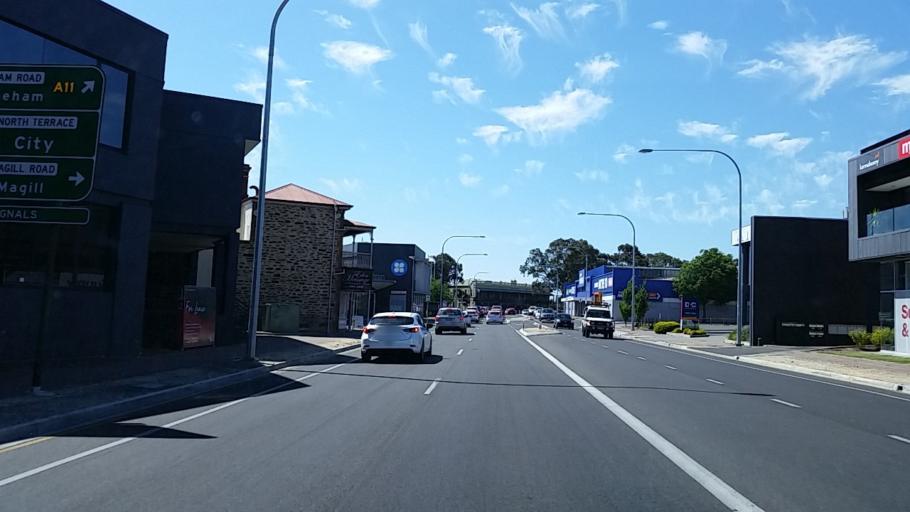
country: AU
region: South Australia
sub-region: Norwood Payneham St Peters
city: Trinity Gardens
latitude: -34.9176
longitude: 138.6229
